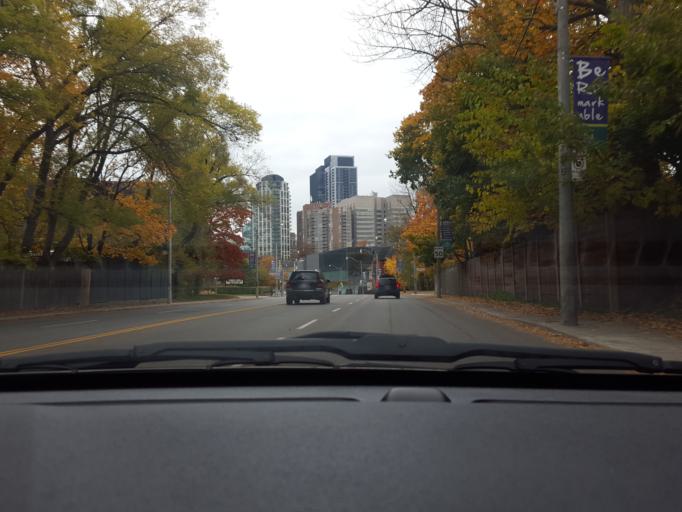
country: CA
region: Ontario
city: Toronto
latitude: 43.6771
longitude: -79.3807
